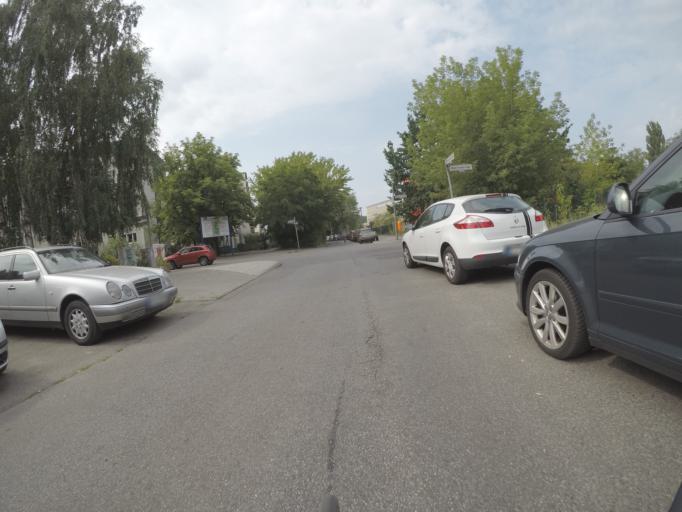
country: DE
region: Berlin
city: Buch
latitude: 52.6337
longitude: 13.4946
